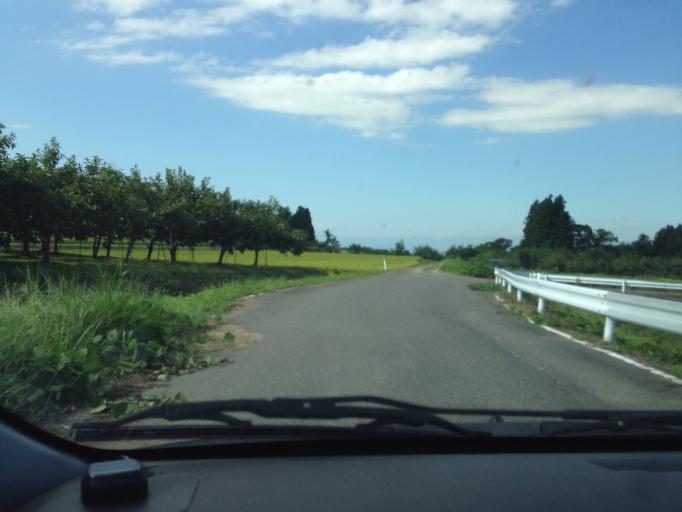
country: JP
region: Fukushima
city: Kitakata
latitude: 37.4473
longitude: 139.8179
